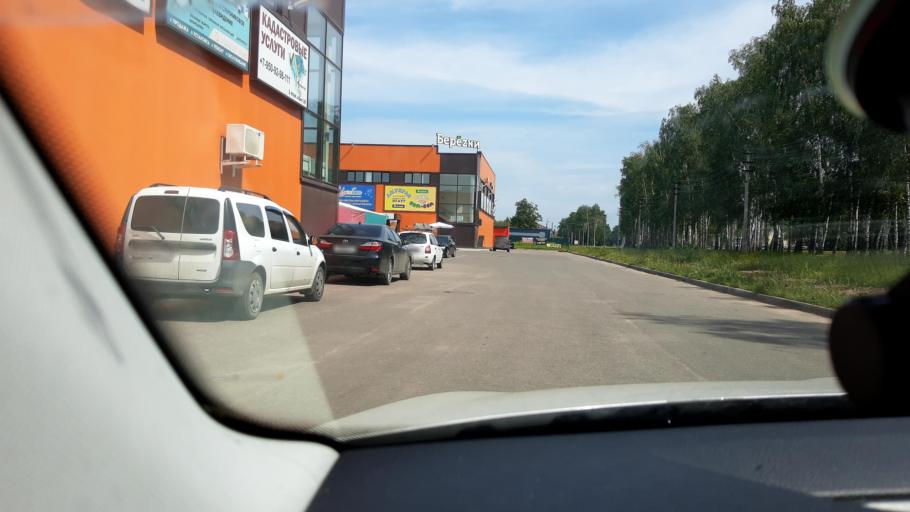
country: RU
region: Tula
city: Zaokskiy
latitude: 54.7394
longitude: 37.3689
